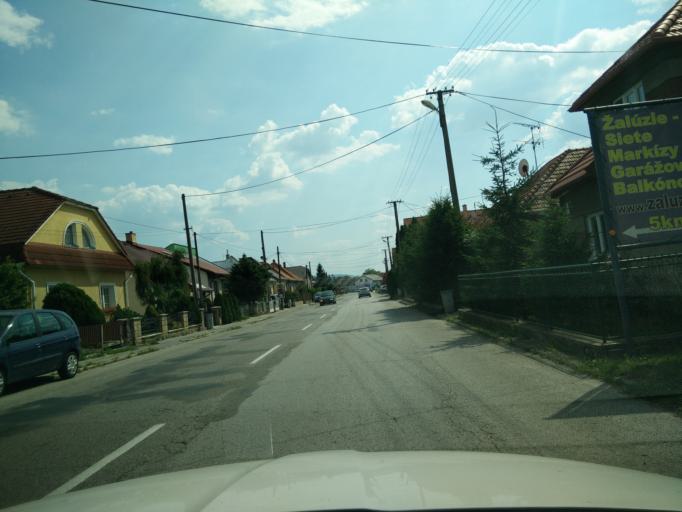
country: SK
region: Nitriansky
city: Partizanske
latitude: 48.6370
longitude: 18.3571
